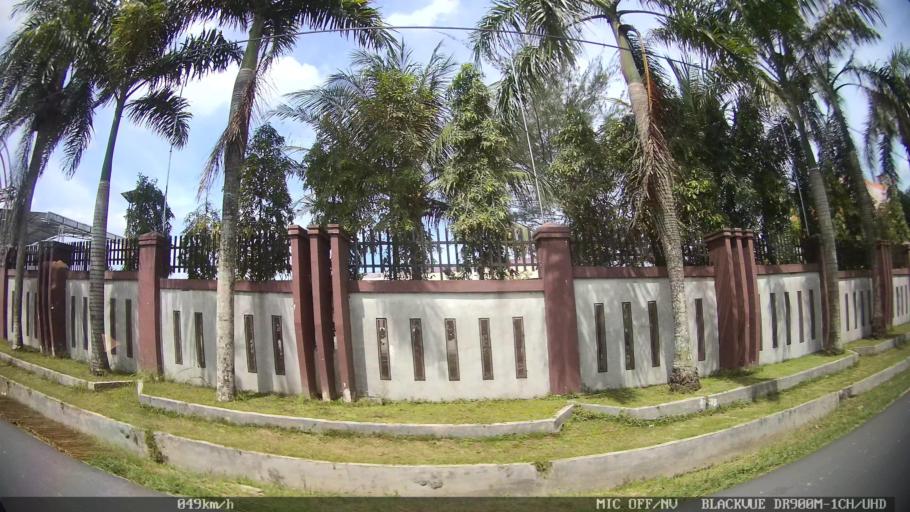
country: ID
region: North Sumatra
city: Percut
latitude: 3.5919
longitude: 98.8616
